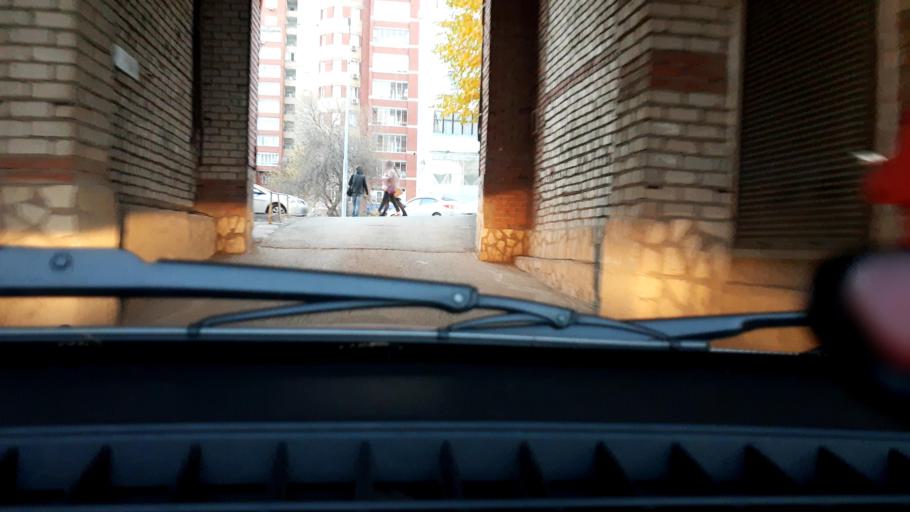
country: RU
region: Bashkortostan
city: Ufa
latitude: 54.7288
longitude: 55.9837
